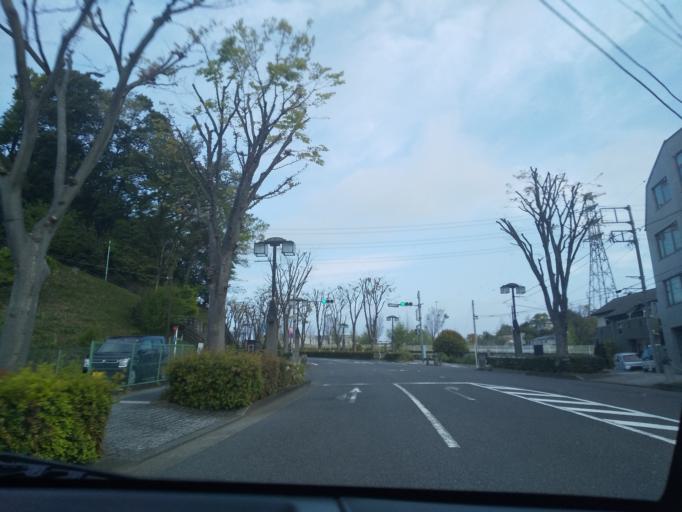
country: JP
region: Tokyo
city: Chofugaoka
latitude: 35.6387
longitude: 139.4975
